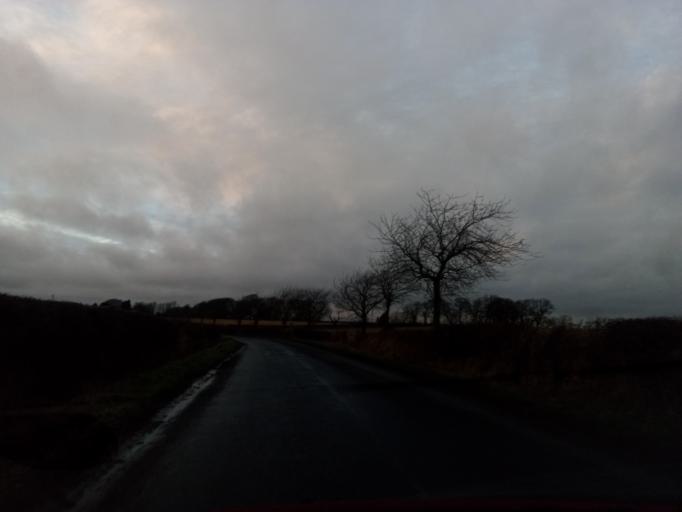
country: GB
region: England
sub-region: Northumberland
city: Meldon
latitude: 55.1328
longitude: -1.7986
